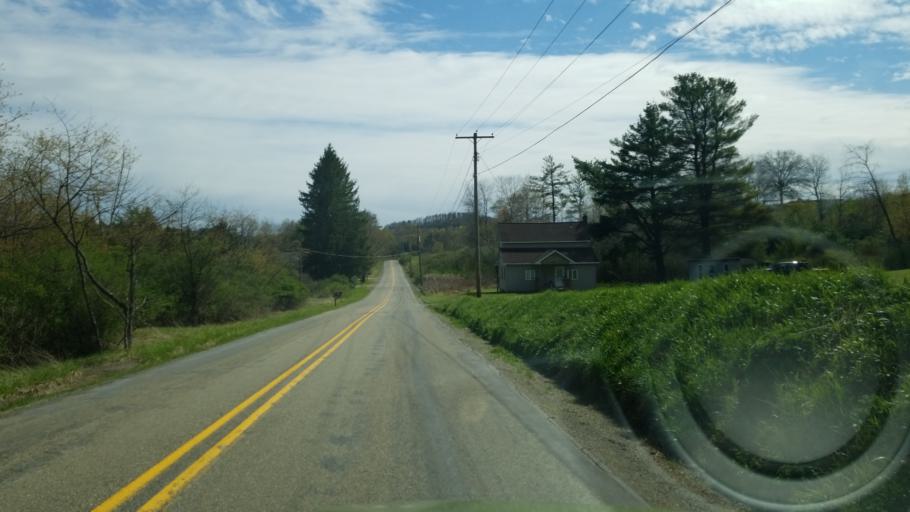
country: US
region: Pennsylvania
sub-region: Jefferson County
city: Brockway
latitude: 41.2299
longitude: -78.8509
